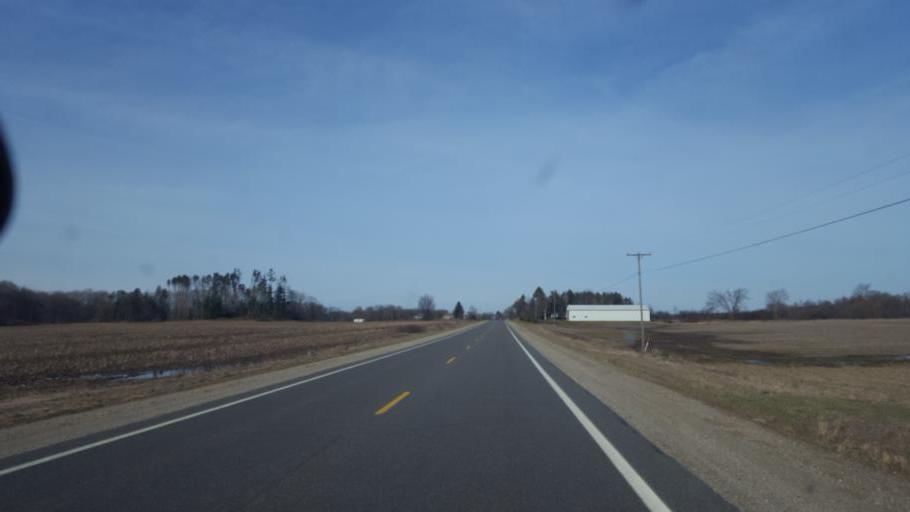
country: US
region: Michigan
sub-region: Montcalm County
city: Lakeview
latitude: 43.4327
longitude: -85.3672
